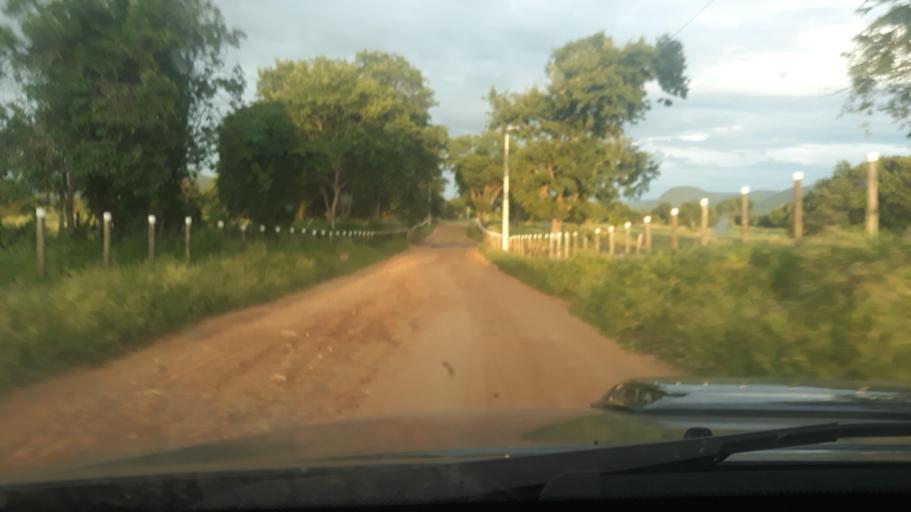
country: BR
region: Bahia
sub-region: Riacho De Santana
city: Riacho de Santana
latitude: -13.9005
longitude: -42.8839
